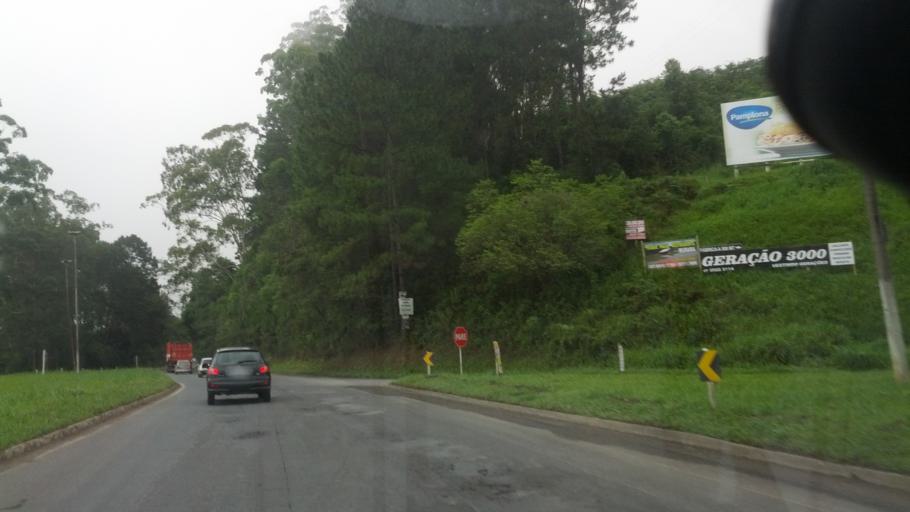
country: BR
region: Santa Catarina
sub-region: Rio Do Sul
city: Rio do Sul
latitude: -27.2459
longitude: -49.6943
